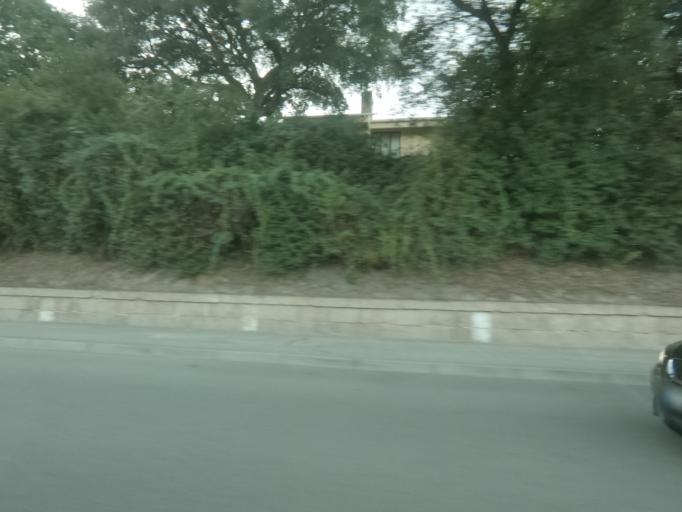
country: PT
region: Vila Real
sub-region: Vila Real
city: Vila Real
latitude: 41.3064
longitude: -7.7396
